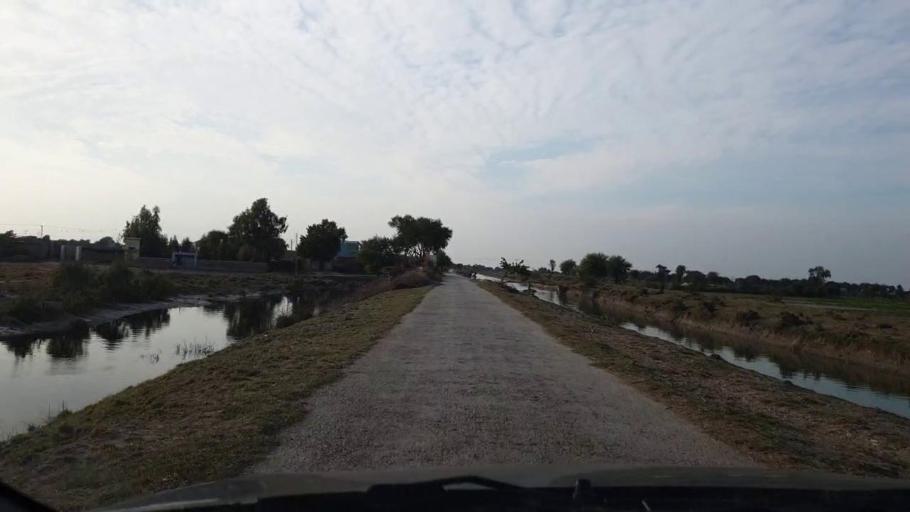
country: PK
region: Sindh
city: Jhol
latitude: 25.9539
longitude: 68.8508
